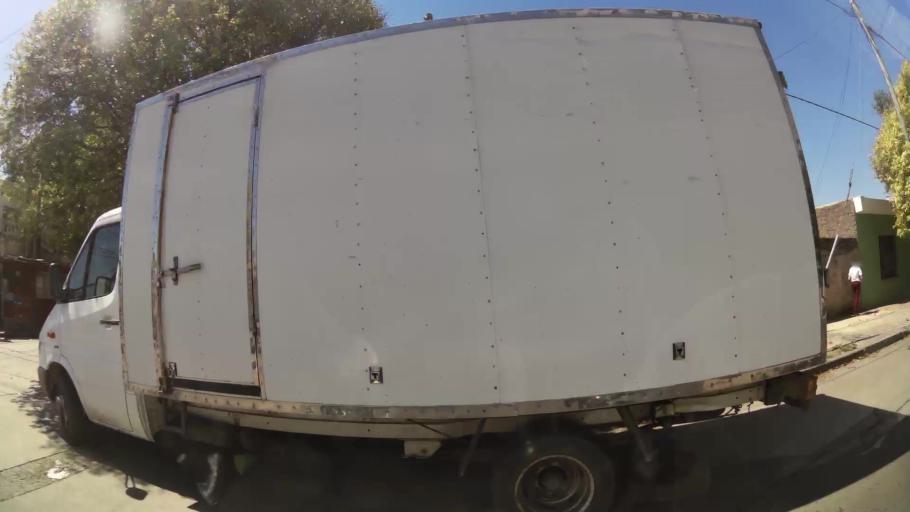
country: AR
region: Cordoba
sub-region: Departamento de Capital
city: Cordoba
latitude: -31.3777
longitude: -64.1430
